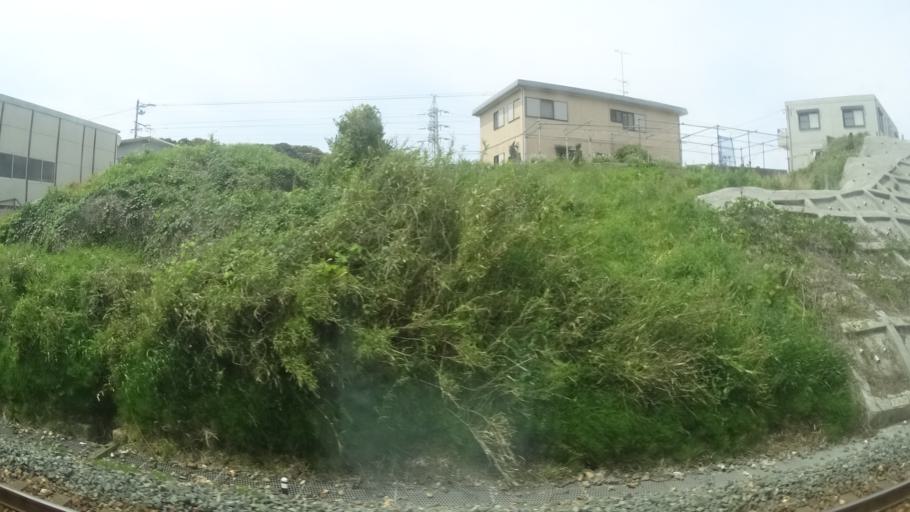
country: JP
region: Shizuoka
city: Kosai-shi
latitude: 34.7211
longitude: 137.5380
